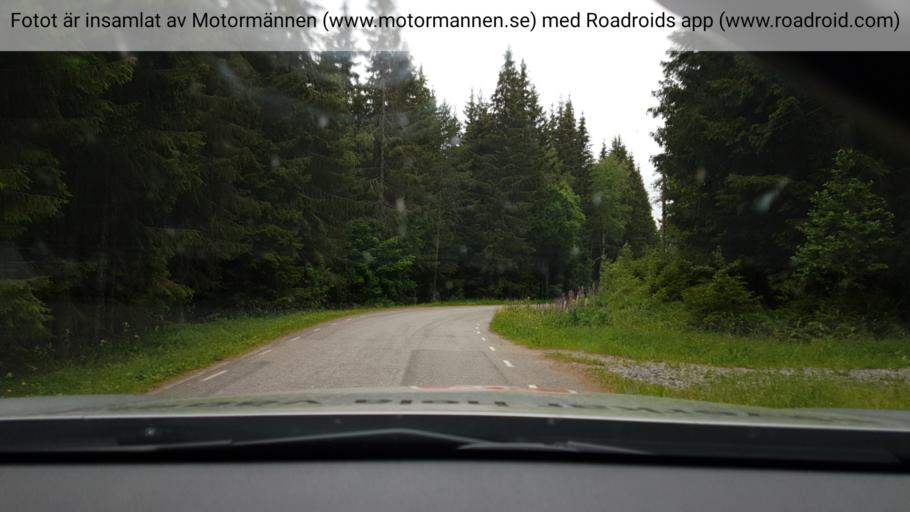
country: SE
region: Joenkoeping
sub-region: Mullsjo Kommun
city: Mullsjoe
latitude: 57.9533
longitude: 13.6714
